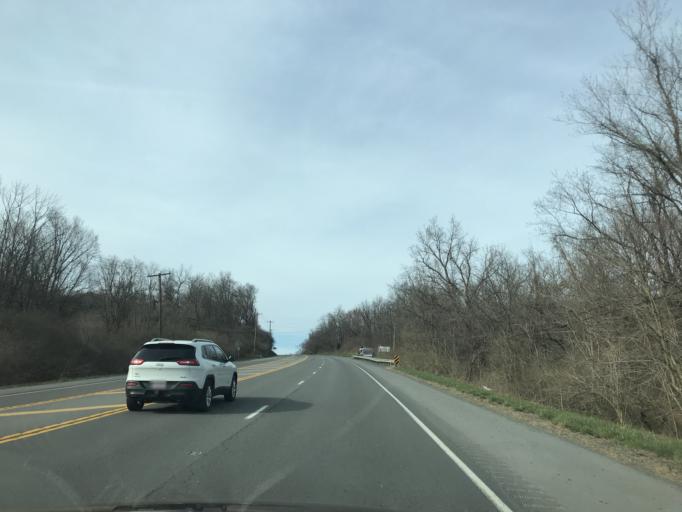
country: US
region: Pennsylvania
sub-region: Lycoming County
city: Montgomery
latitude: 41.1552
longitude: -76.9085
